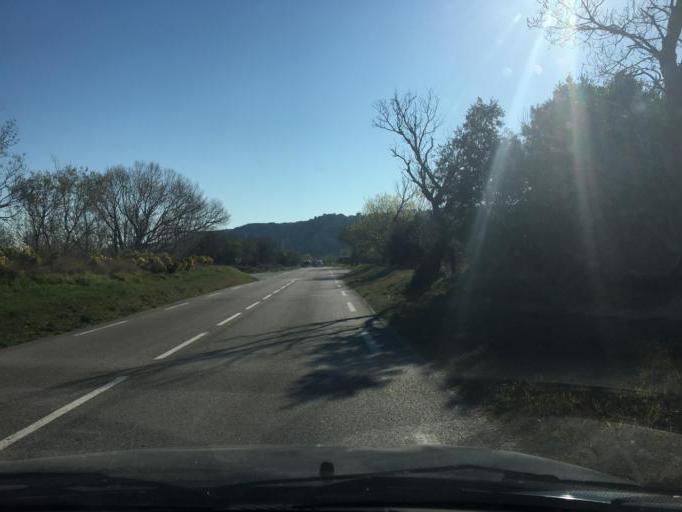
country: FR
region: Languedoc-Roussillon
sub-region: Departement du Gard
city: Les Angles
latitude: 43.9769
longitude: 4.7430
